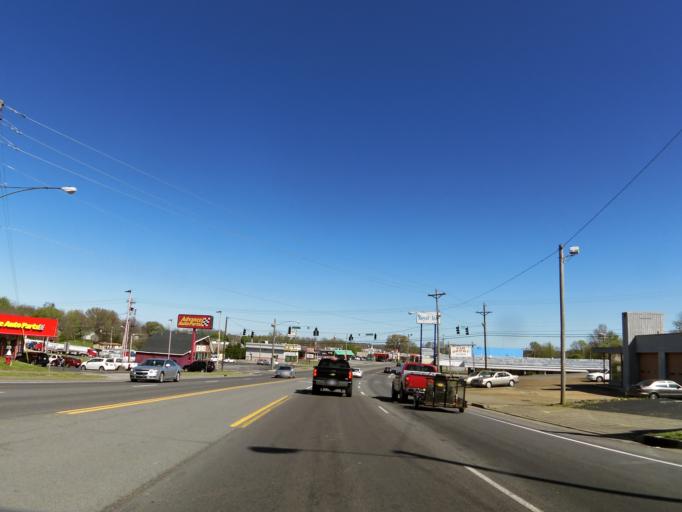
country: US
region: Tennessee
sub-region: Robertson County
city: Springfield
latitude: 36.4979
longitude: -86.8818
